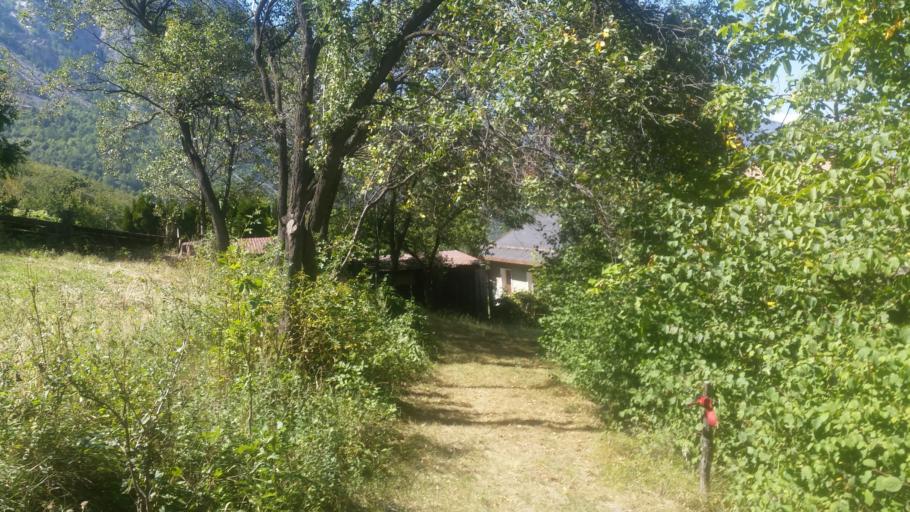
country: FR
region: Rhone-Alpes
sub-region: Departement de la Savoie
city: Villargondran
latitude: 45.2467
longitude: 6.4004
